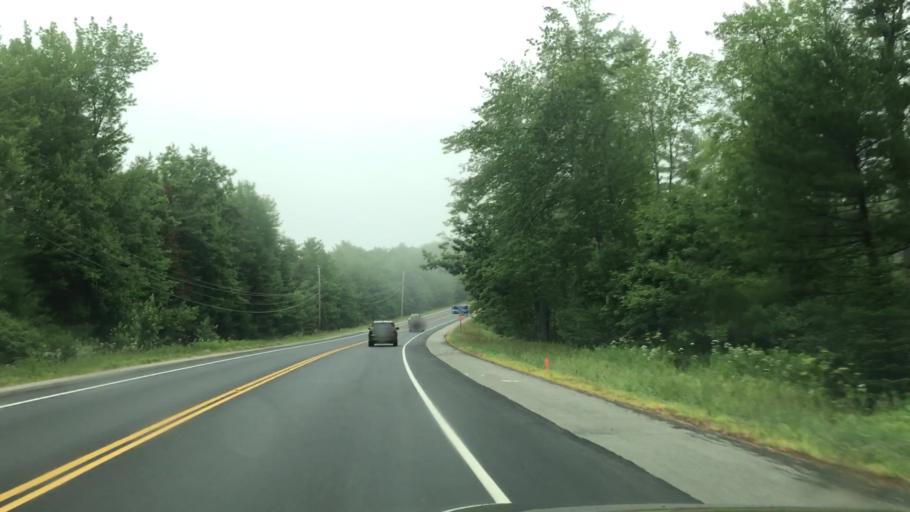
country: US
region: Maine
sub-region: Lincoln County
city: Waldoboro
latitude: 44.1080
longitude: -69.3584
